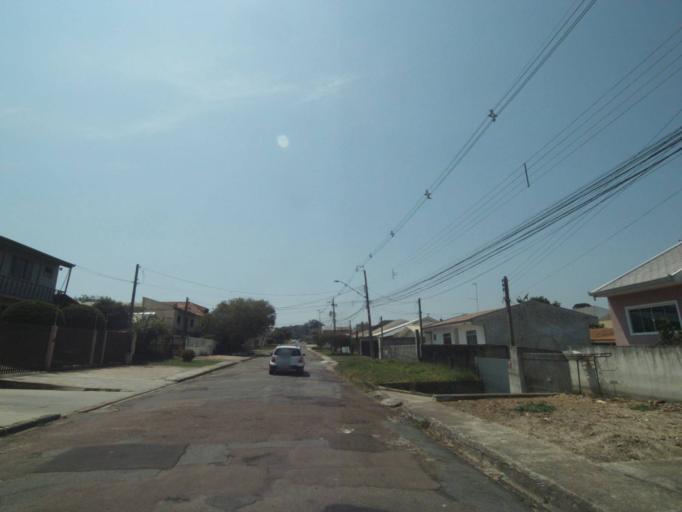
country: BR
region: Parana
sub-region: Sao Jose Dos Pinhais
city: Sao Jose dos Pinhais
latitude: -25.5162
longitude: -49.2666
